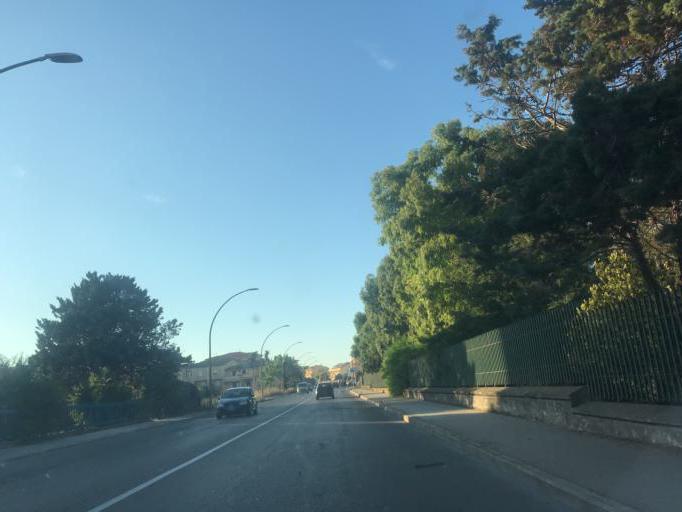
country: IT
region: Sardinia
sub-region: Provincia di Sassari
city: Alghero
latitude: 40.5802
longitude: 8.3187
